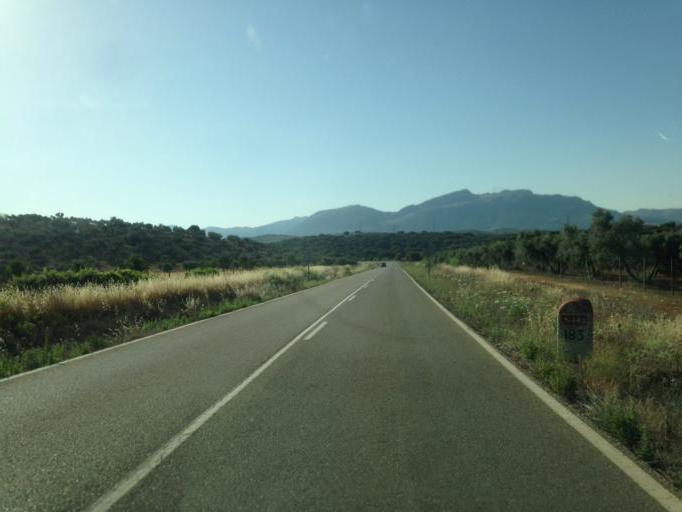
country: ES
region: Andalusia
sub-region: Provincia de Malaga
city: Archidona
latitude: 37.1139
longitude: -4.3345
